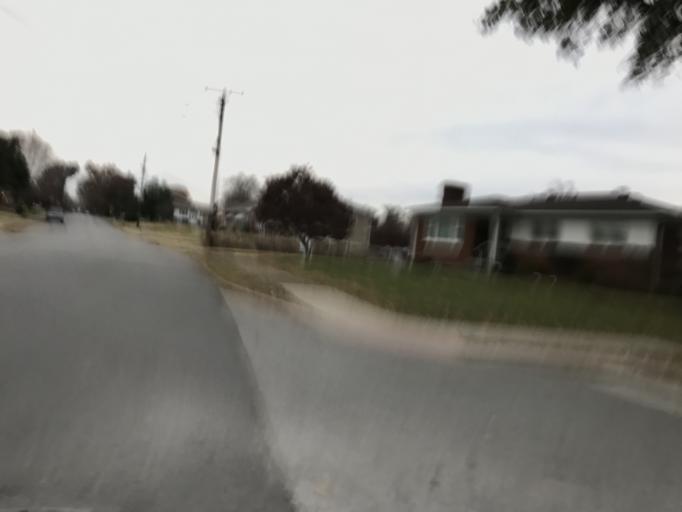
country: US
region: Kentucky
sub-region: Jefferson County
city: Audubon Park
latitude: 38.2094
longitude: -85.7328
